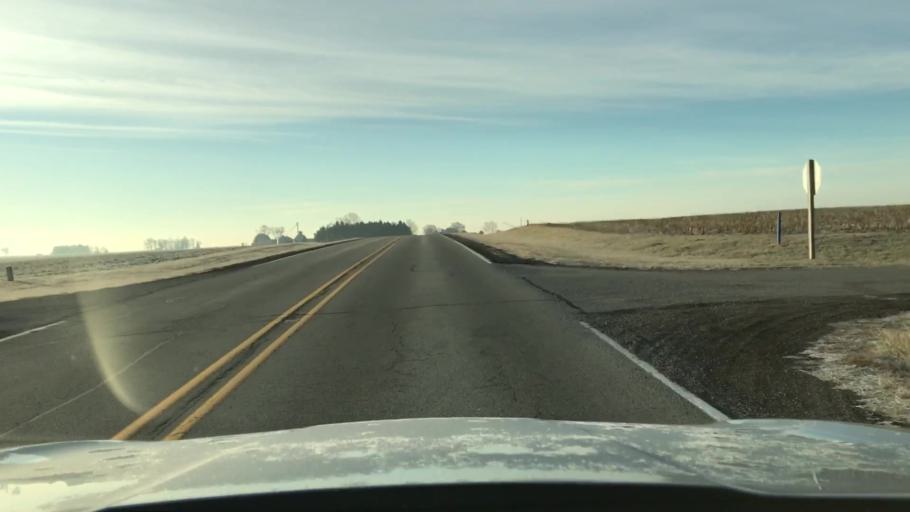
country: US
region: Illinois
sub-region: McLean County
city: Hudson
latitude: 40.6203
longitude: -88.9455
